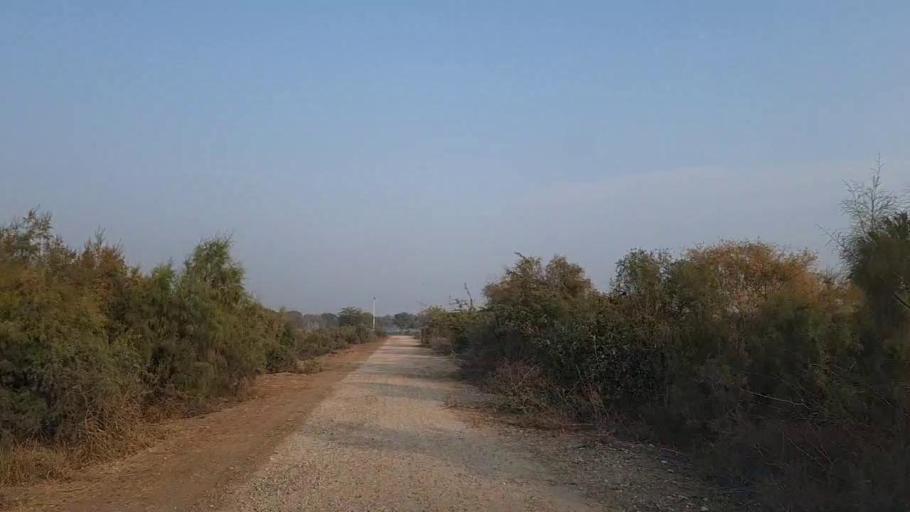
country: PK
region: Sindh
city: Jam Sahib
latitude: 26.3204
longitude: 68.5974
